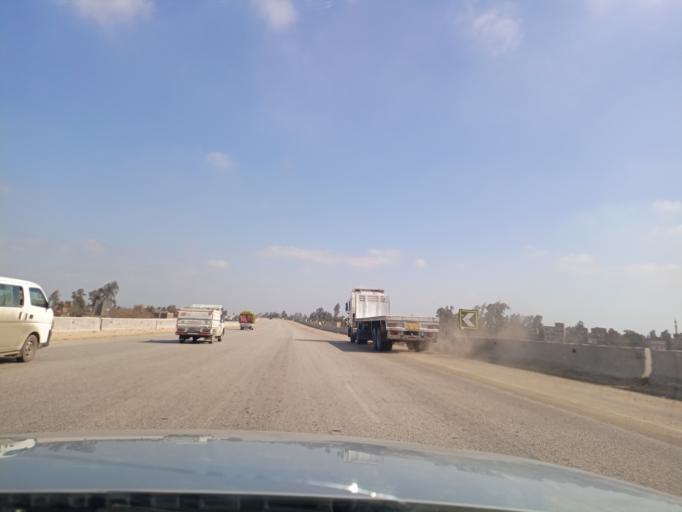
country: EG
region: Muhafazat al Minufiyah
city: Al Bajur
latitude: 30.4224
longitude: 31.0863
